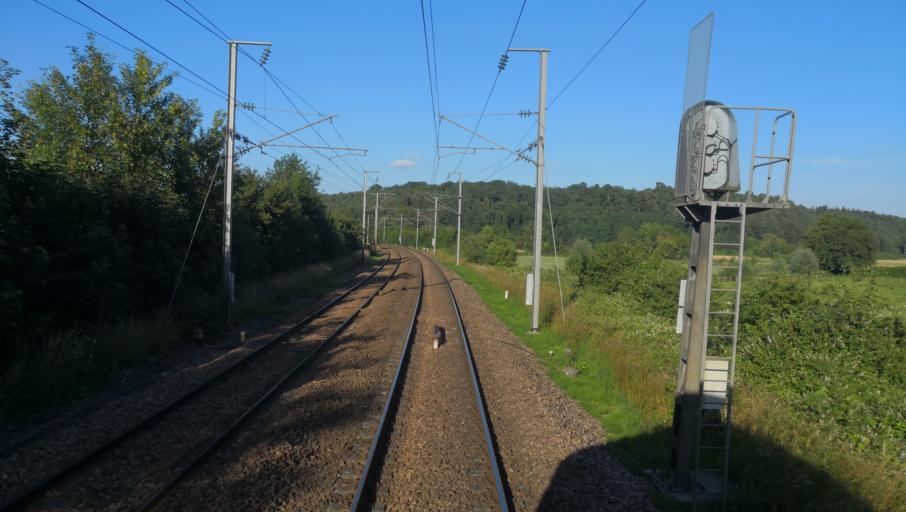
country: FR
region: Haute-Normandie
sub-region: Departement de l'Eure
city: Conches-en-Ouche
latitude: 48.9770
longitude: 1.0061
